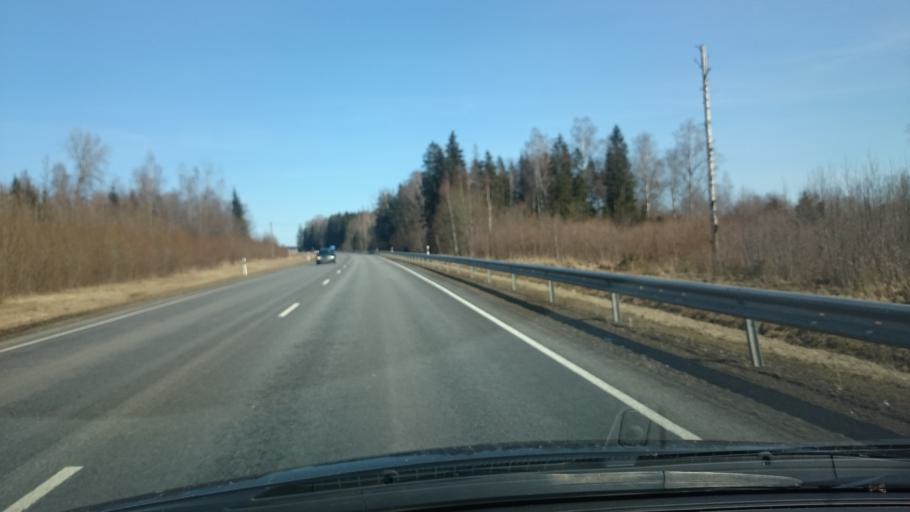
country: EE
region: Paernumaa
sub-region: Vaendra vald (alev)
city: Vandra
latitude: 58.6481
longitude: 24.9885
